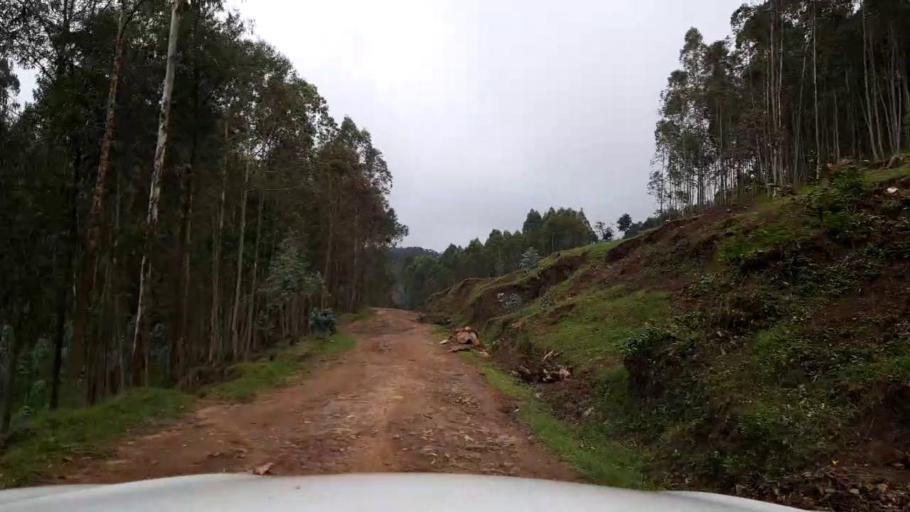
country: RW
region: Northern Province
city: Musanze
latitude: -1.6078
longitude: 29.7673
